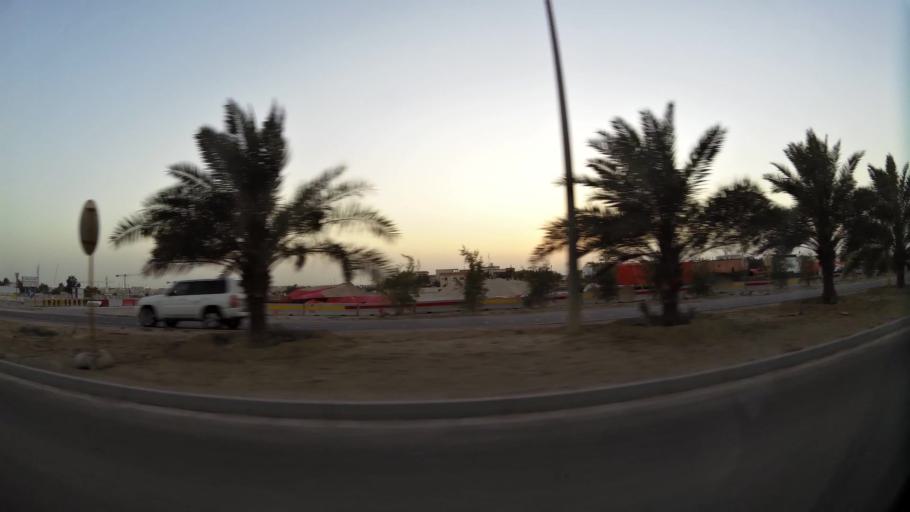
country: QA
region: Baladiyat ar Rayyan
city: Ar Rayyan
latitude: 25.3061
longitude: 51.4644
